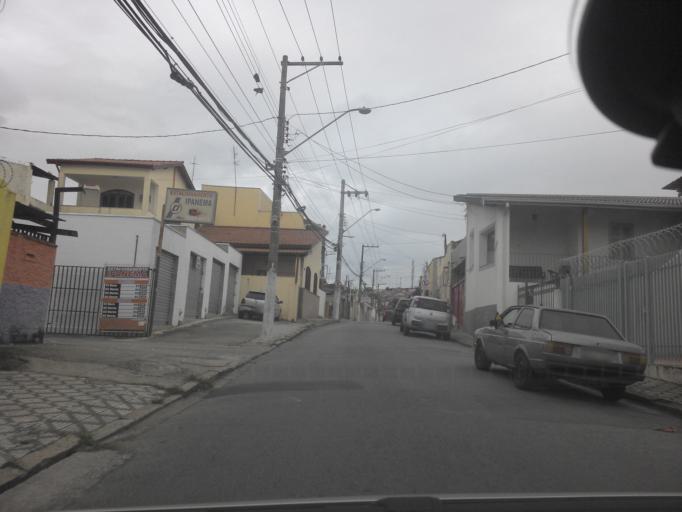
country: BR
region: Sao Paulo
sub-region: Taubate
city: Taubate
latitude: -23.0273
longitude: -45.5513
